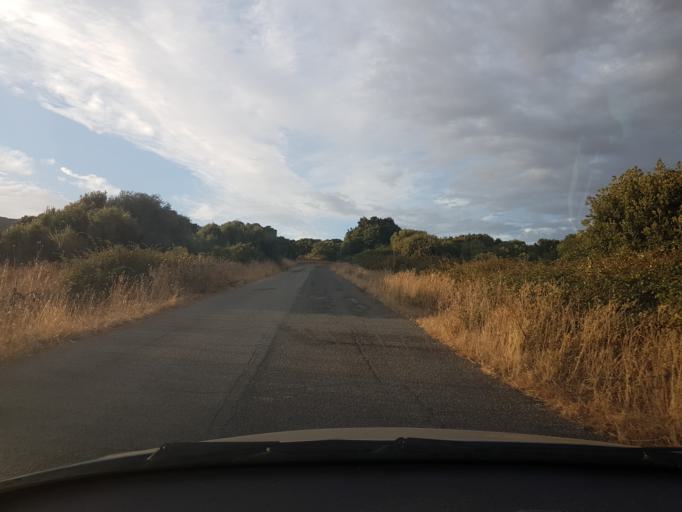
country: IT
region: Sardinia
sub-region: Provincia di Oristano
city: Seneghe
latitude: 40.0999
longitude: 8.6210
